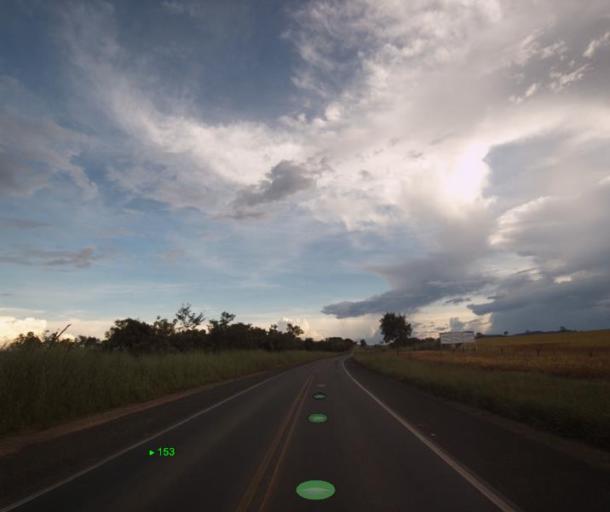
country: BR
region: Goias
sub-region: Uruacu
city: Uruacu
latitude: -14.1126
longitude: -49.1044
